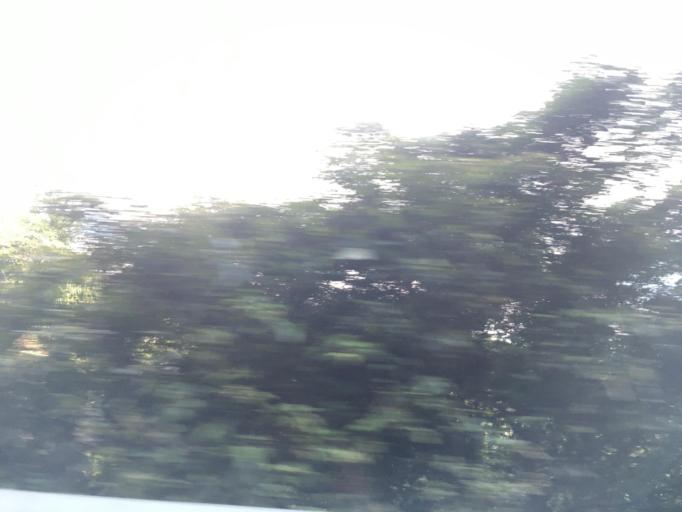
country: TW
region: Taiwan
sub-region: Yilan
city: Yilan
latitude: 24.7512
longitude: 121.6426
